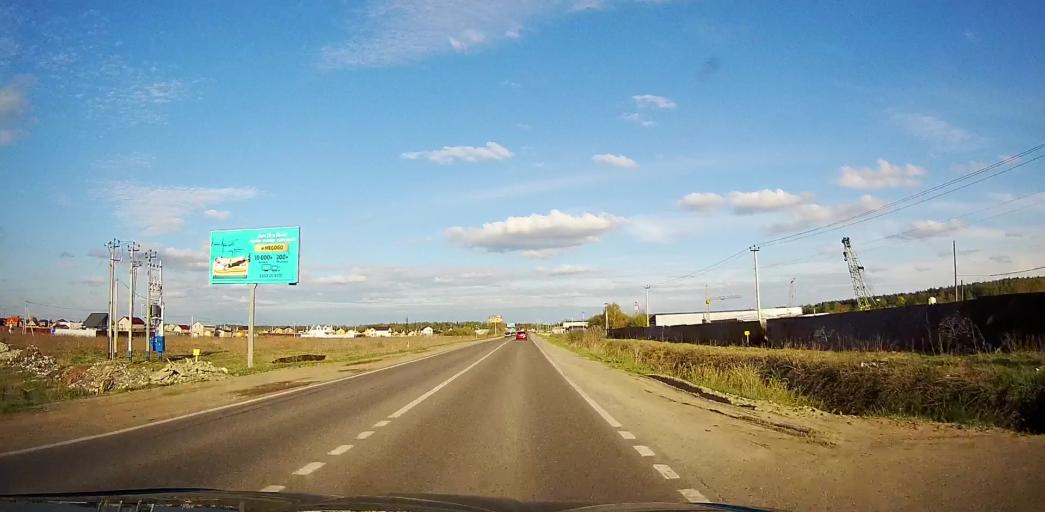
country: RU
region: Moskovskaya
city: Malyshevo
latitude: 55.4858
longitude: 38.3307
